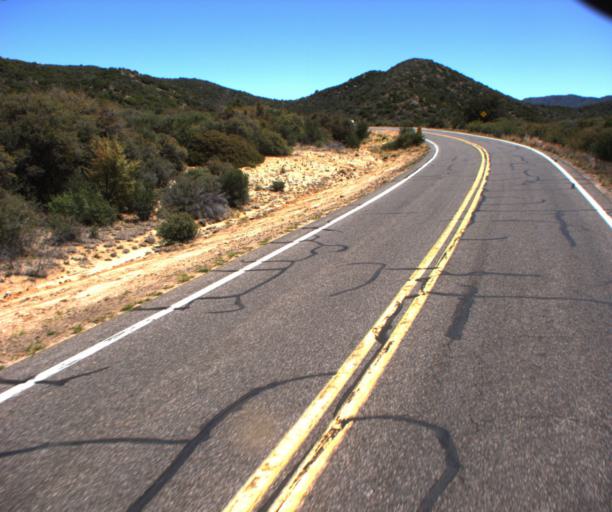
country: US
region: Arizona
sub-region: Yavapai County
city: Prescott
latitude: 34.4234
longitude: -112.5585
